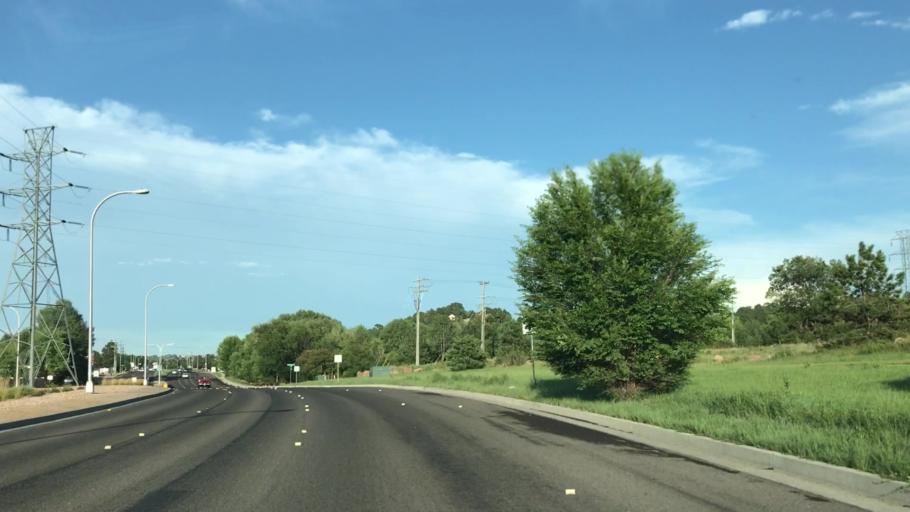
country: US
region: Colorado
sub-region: El Paso County
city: Colorado Springs
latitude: 38.8889
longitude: -104.7755
